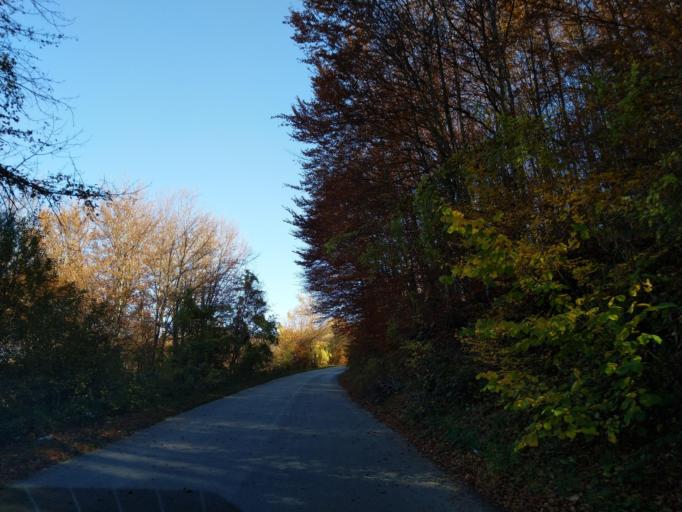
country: RS
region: Central Serbia
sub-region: Zlatiborski Okrug
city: Cajetina
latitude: 43.6796
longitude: 19.8459
